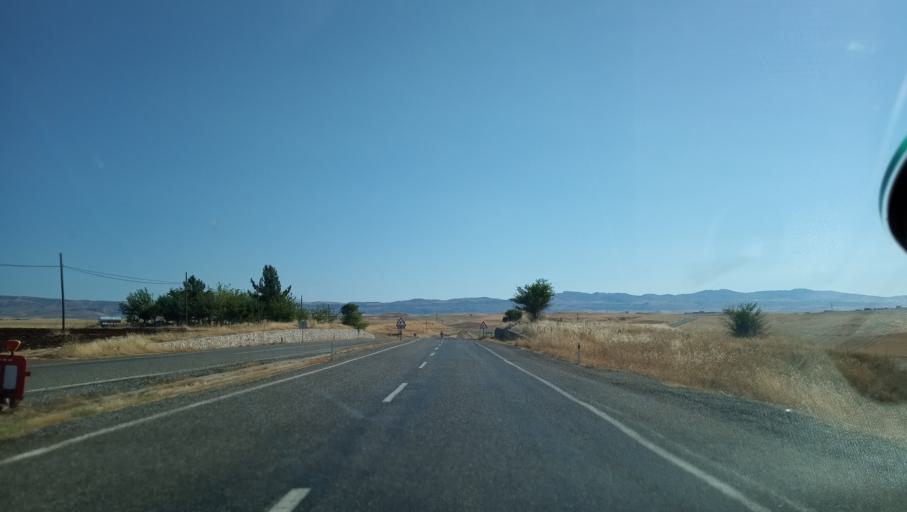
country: TR
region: Diyarbakir
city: Bagdere
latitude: 38.1211
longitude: 40.7414
